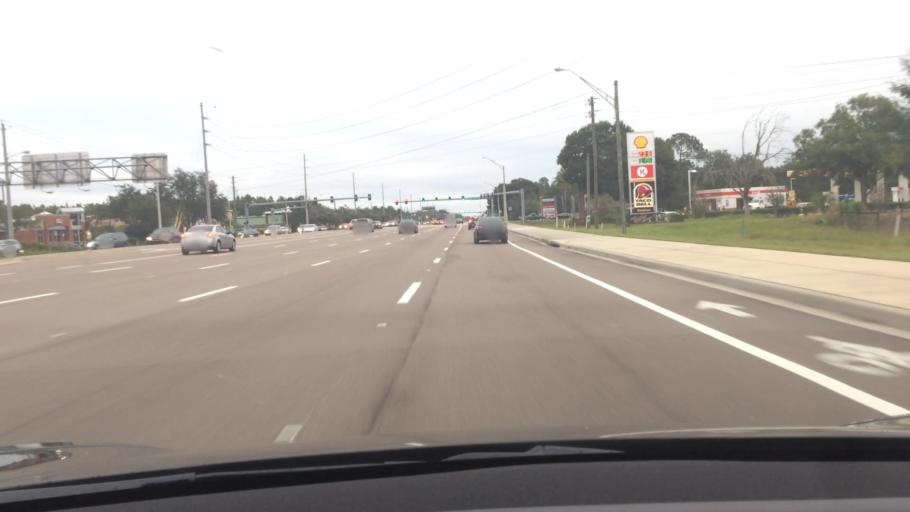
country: US
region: Florida
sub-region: Hillsborough County
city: Pebble Creek
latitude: 28.1253
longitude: -82.3706
